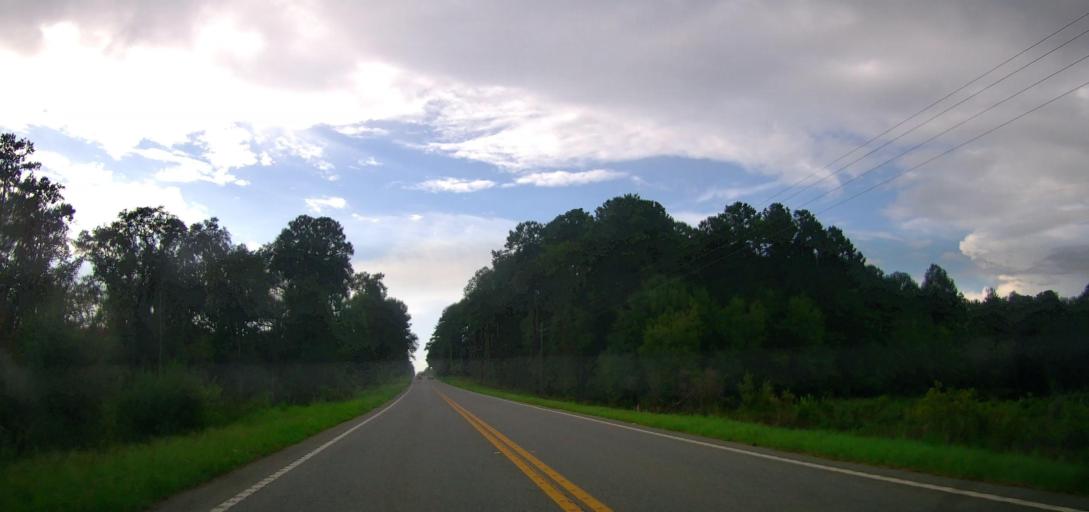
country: US
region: Georgia
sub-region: Ware County
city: Deenwood
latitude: 31.3102
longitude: -82.5665
